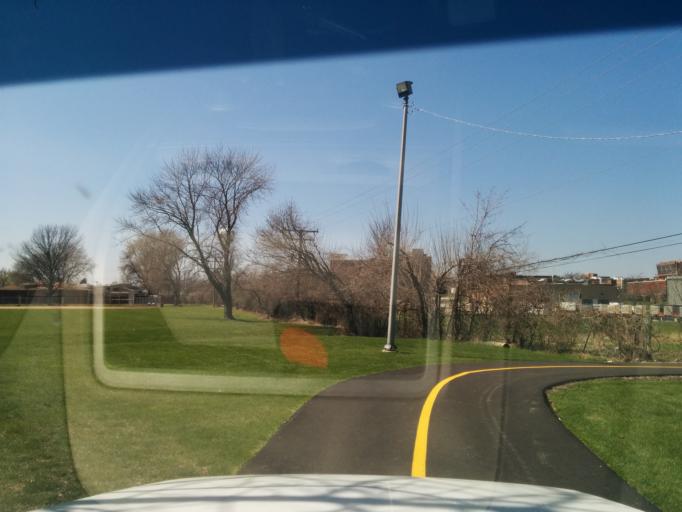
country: US
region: Illinois
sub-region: Cook County
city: Oak Forest
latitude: 41.5959
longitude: -87.7285
